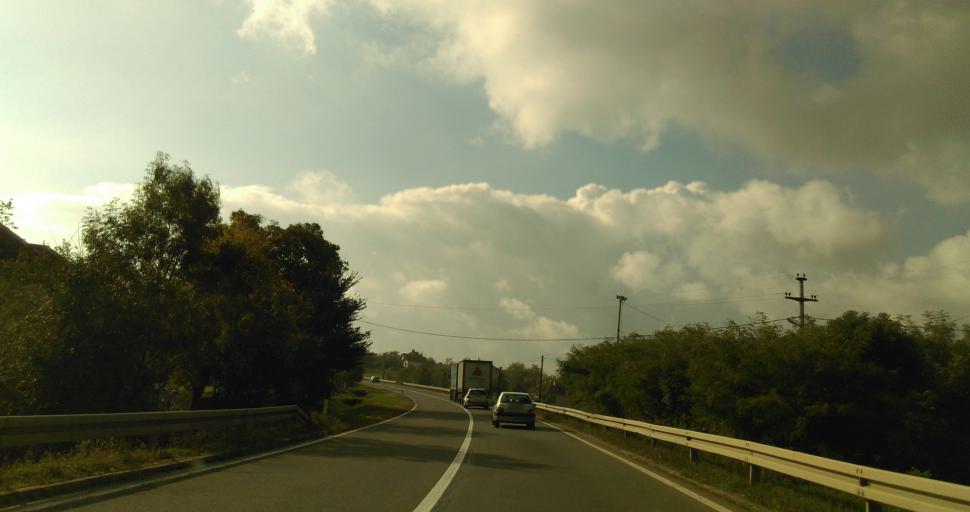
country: RS
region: Central Serbia
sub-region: Kolubarski Okrug
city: Lajkovac
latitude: 44.3588
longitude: 20.1898
